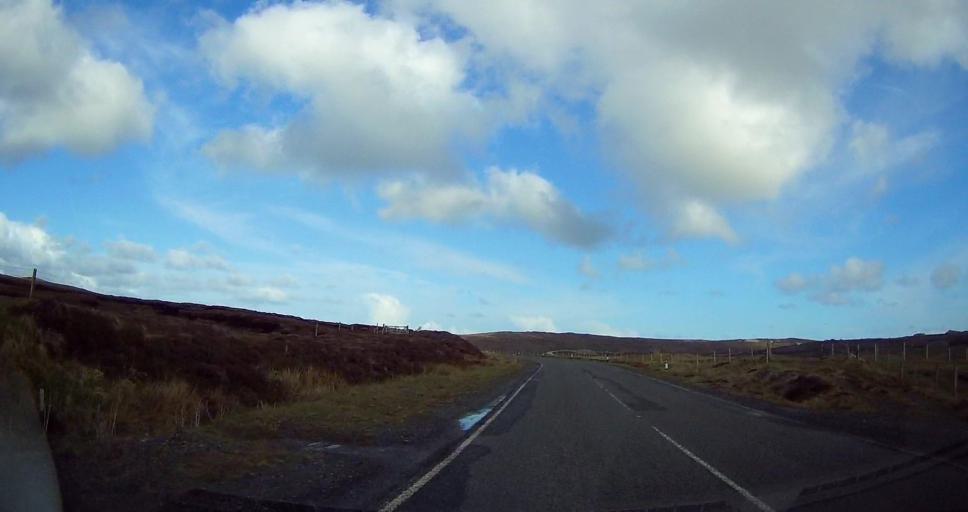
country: GB
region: Scotland
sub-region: Shetland Islands
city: Lerwick
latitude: 60.3493
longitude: -1.2310
